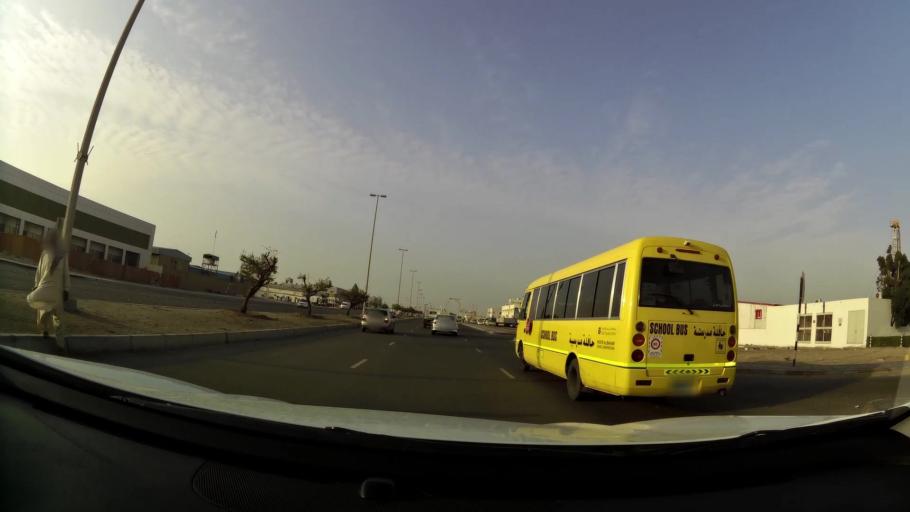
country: AE
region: Abu Dhabi
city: Abu Dhabi
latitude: 24.3694
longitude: 54.5013
